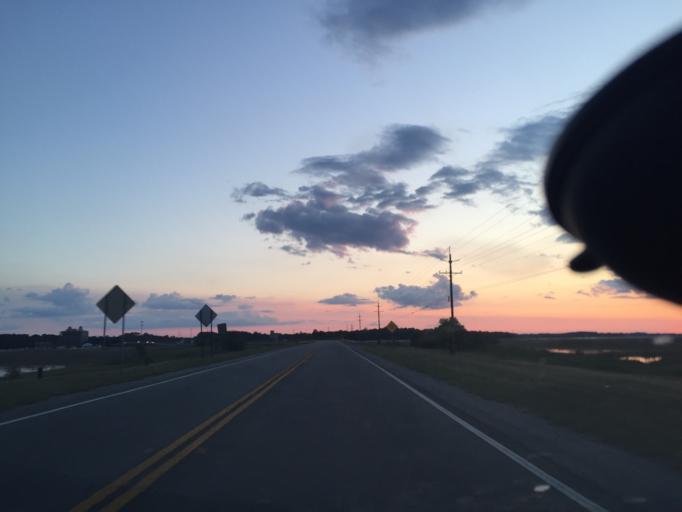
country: US
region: Georgia
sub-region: Chatham County
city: Wilmington Island
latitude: 32.0408
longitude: -80.9496
